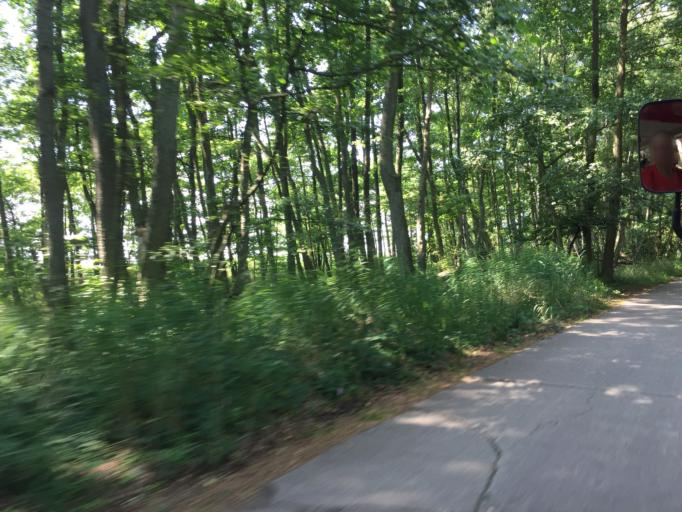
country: PL
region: Pomeranian Voivodeship
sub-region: Powiat leborski
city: Leba
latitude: 54.7523
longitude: 17.4832
